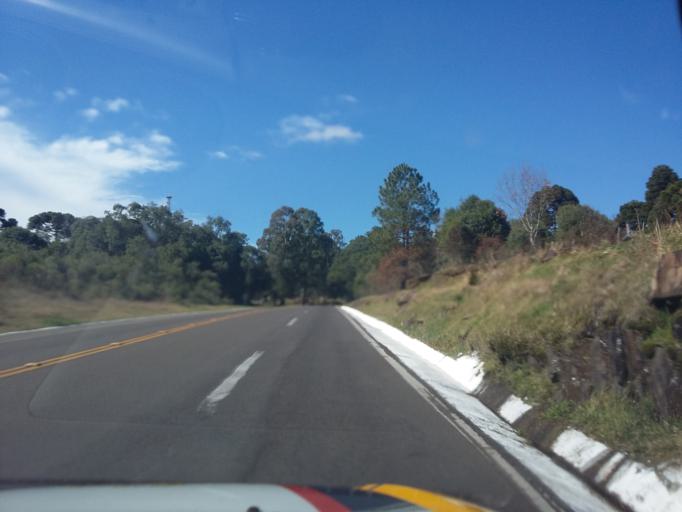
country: BR
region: Rio Grande do Sul
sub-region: Vacaria
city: Vacaria
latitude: -28.5689
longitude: -51.0033
